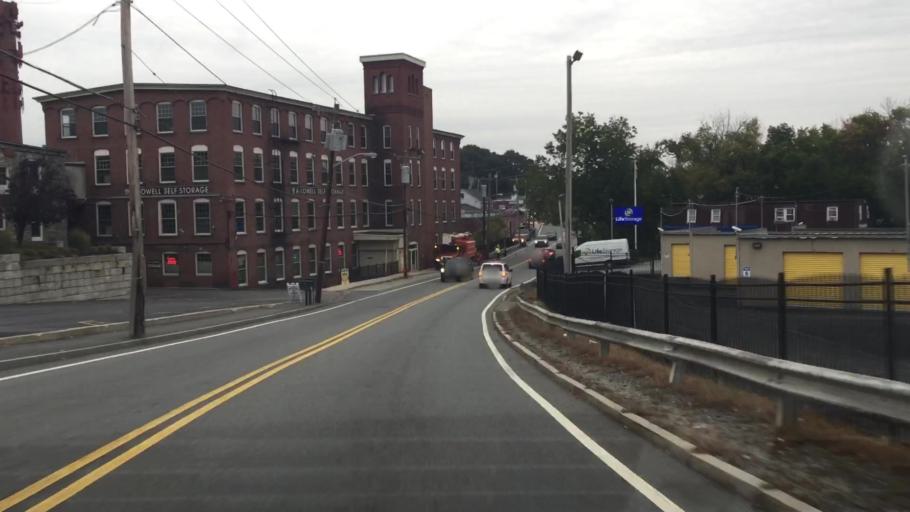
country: US
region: Massachusetts
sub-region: Middlesex County
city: Dracut
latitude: 42.6631
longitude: -71.3259
